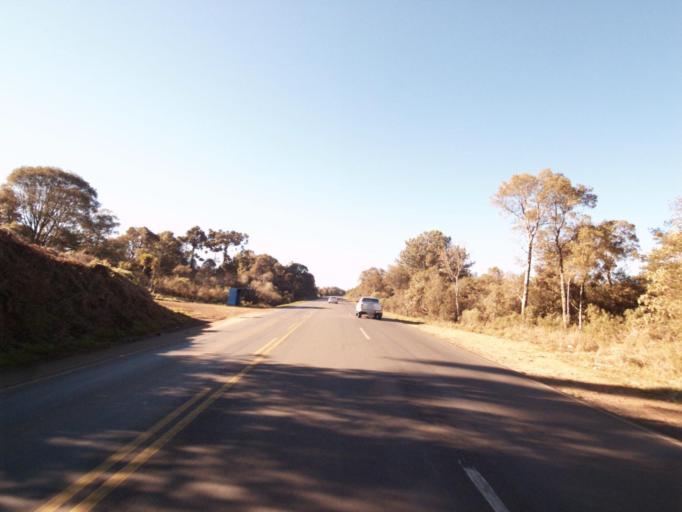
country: BR
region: Santa Catarina
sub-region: Concordia
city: Concordia
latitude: -26.9126
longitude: -51.9628
